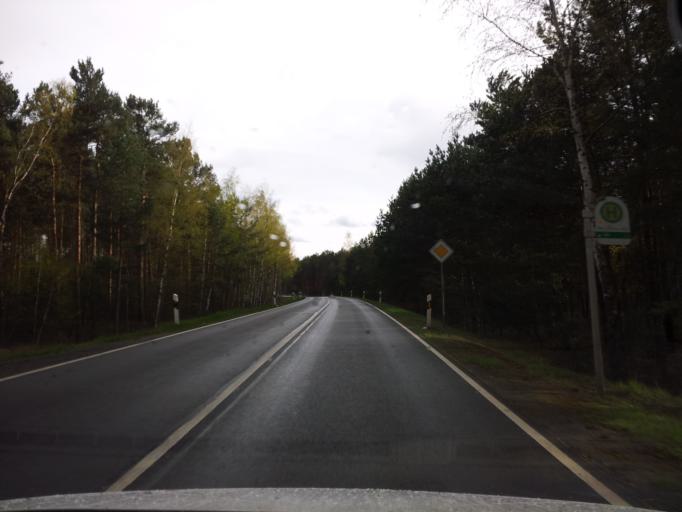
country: DE
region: Brandenburg
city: Heinersbruck
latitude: 51.7414
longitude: 14.4610
